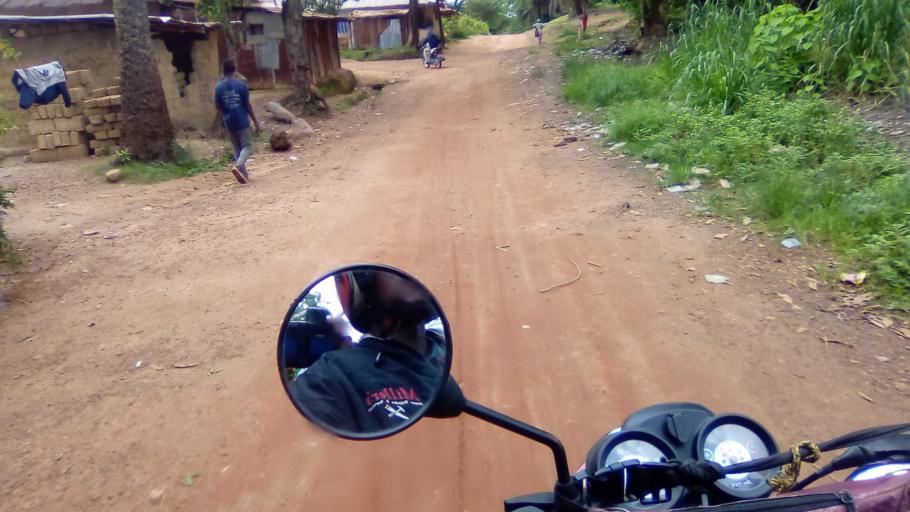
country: SL
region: Southern Province
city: Bo
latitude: 7.9599
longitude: -11.7285
